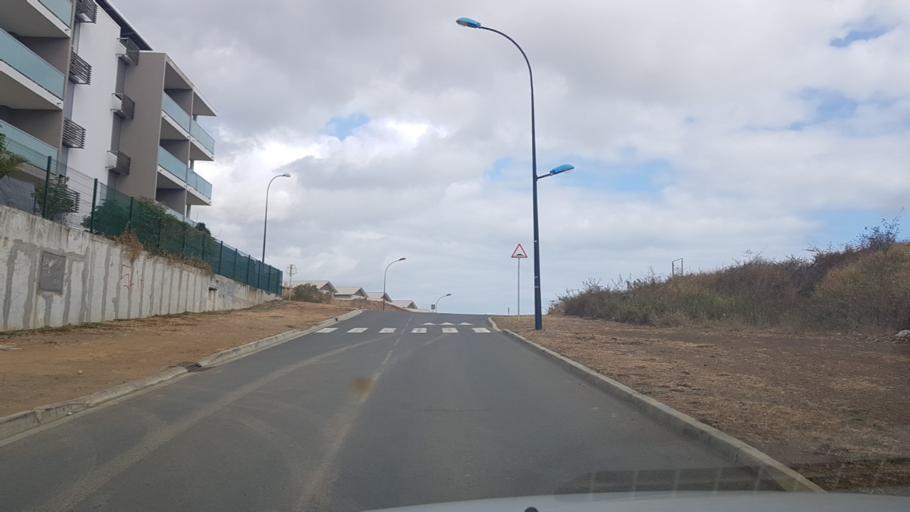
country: NC
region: South Province
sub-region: Dumbea
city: Dumbea
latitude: -22.2031
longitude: 166.4433
